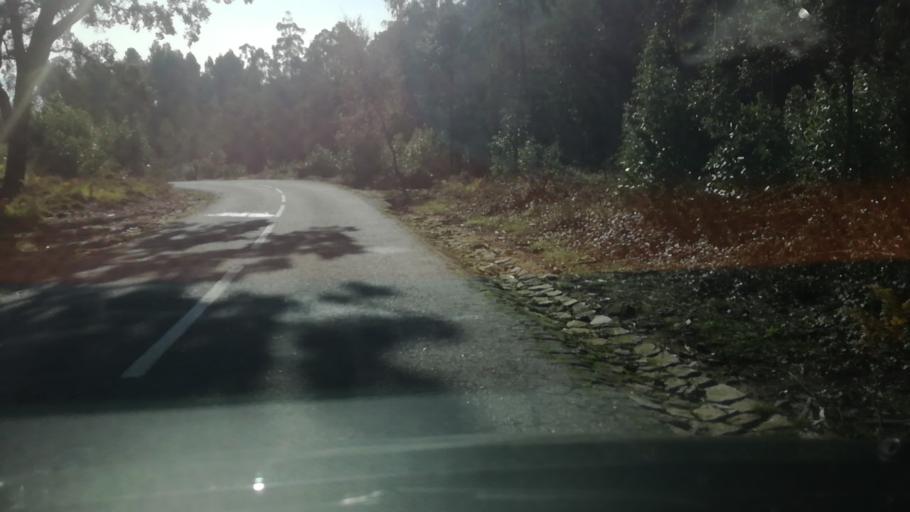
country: PT
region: Braga
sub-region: Braga
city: Braga
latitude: 41.5330
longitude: -8.3565
